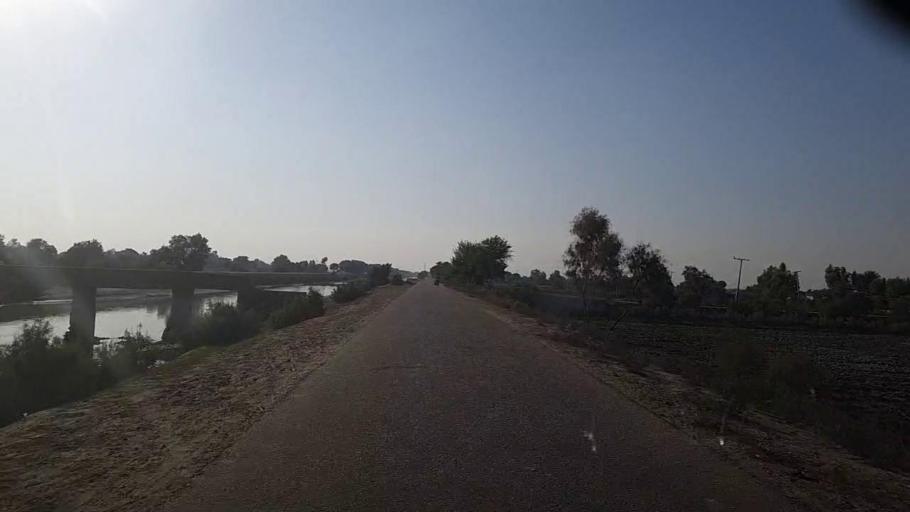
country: PK
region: Sindh
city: Tangwani
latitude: 28.3011
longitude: 68.9492
